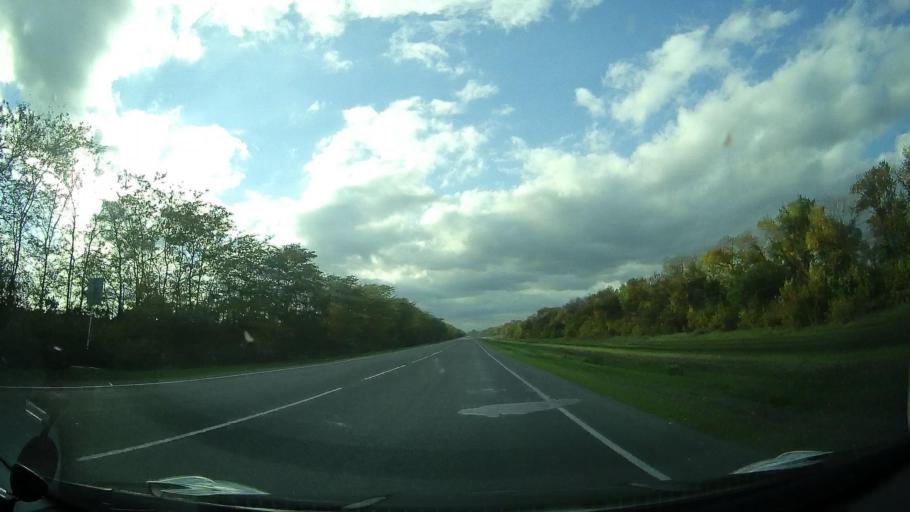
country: RU
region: Rostov
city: Kirovskaya
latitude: 47.0023
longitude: 39.9748
